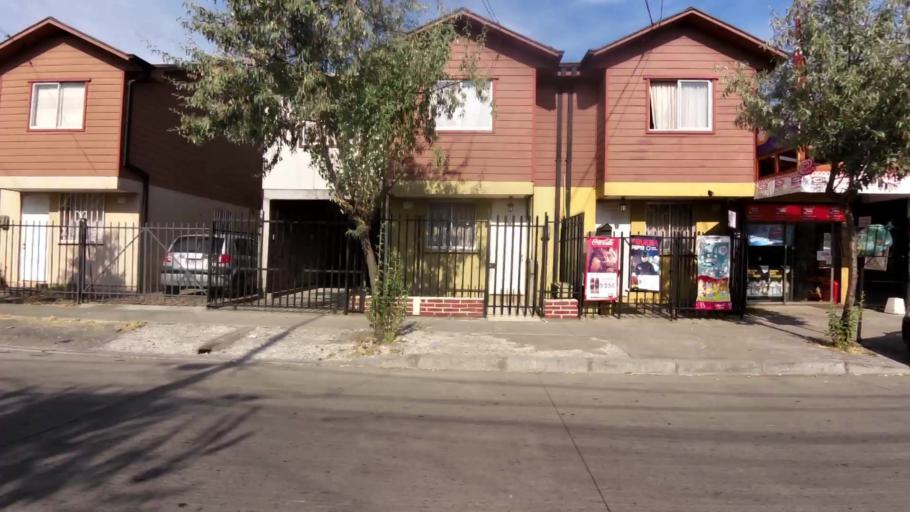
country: CL
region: Biobio
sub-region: Provincia de Concepcion
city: Talcahuano
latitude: -36.7946
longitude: -73.1148
